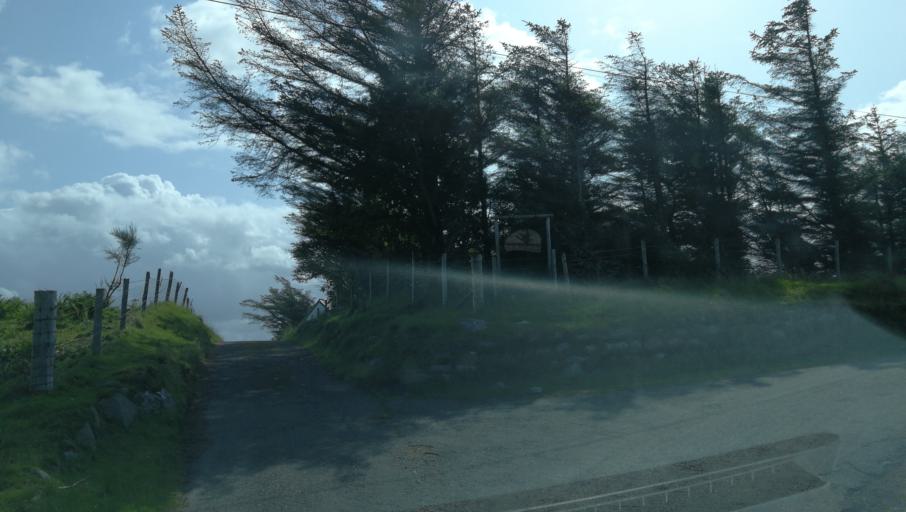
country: GB
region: Scotland
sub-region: Highland
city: Portree
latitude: 57.7461
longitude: -5.7743
